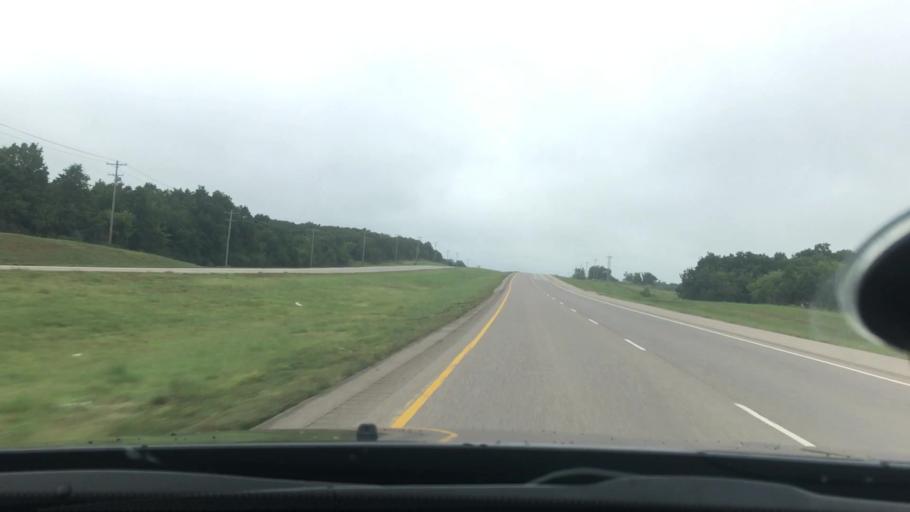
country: US
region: Oklahoma
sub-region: Seminole County
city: Seminole
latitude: 35.3277
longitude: -96.6713
